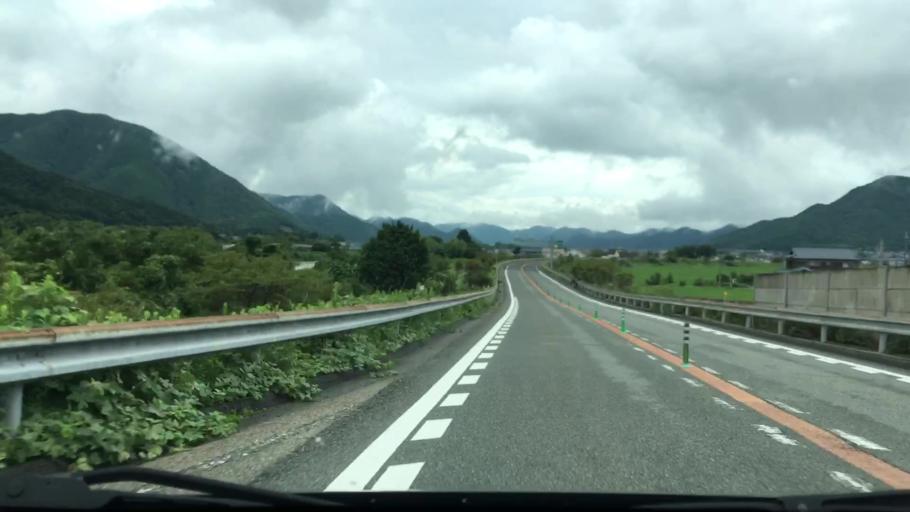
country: JP
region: Hyogo
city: Nishiwaki
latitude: 35.0668
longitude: 134.7683
